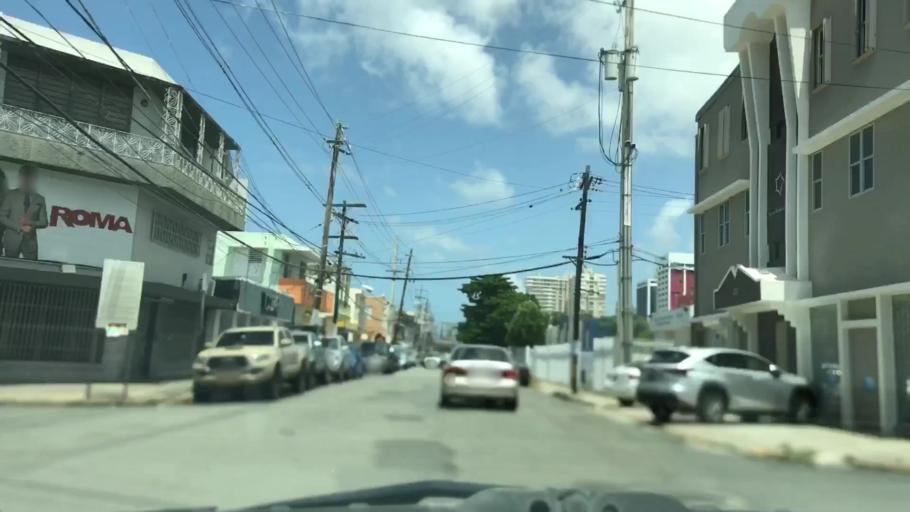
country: PR
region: Catano
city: Catano
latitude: 18.4201
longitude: -66.0625
